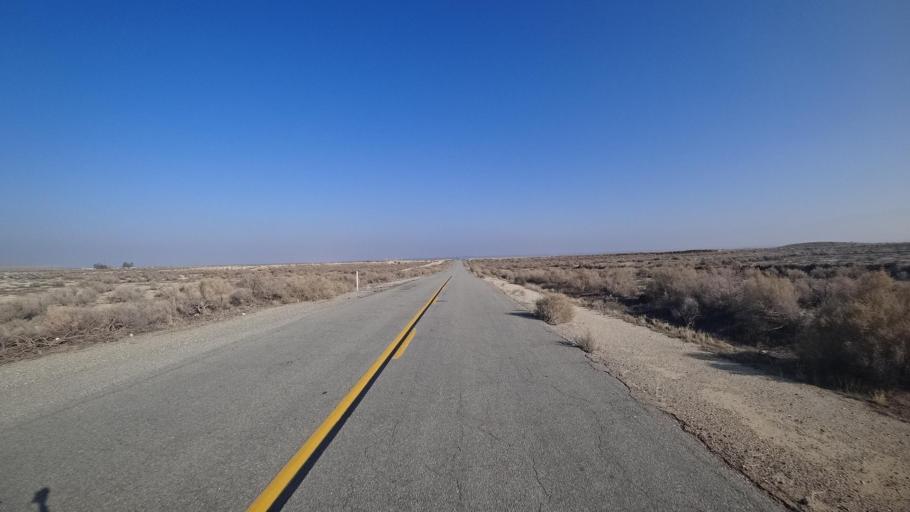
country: US
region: California
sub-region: Kern County
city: Maricopa
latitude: 35.1011
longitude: -119.3827
